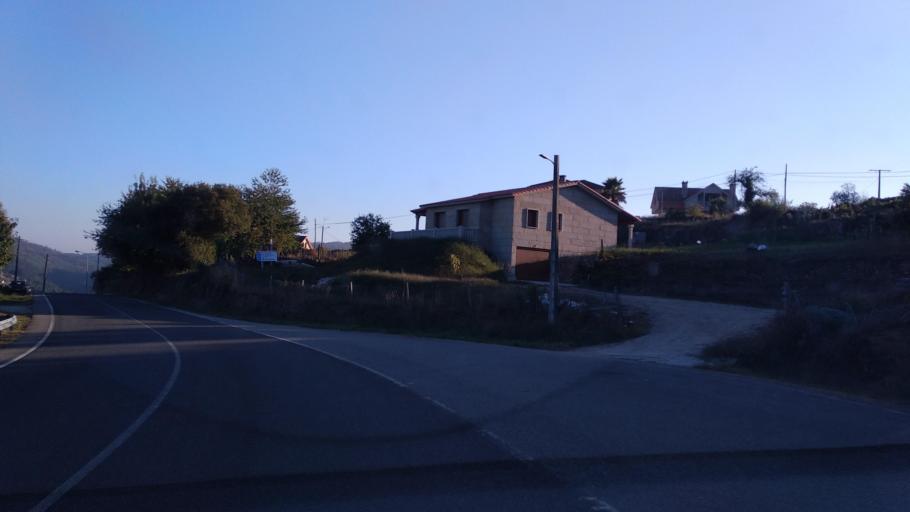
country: ES
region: Galicia
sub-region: Provincia de Pontevedra
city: Ponte Caldelas
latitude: 42.3556
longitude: -8.5427
